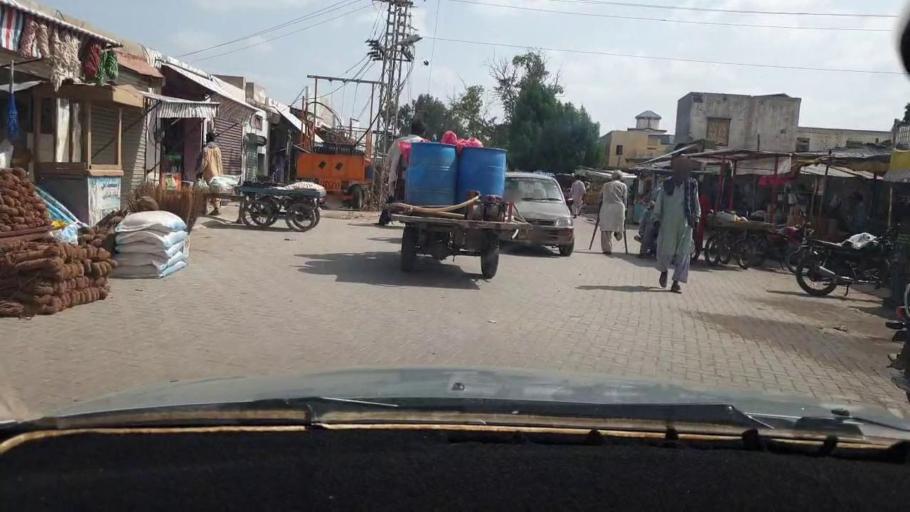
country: PK
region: Sindh
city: Digri
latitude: 25.0702
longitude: 69.2165
